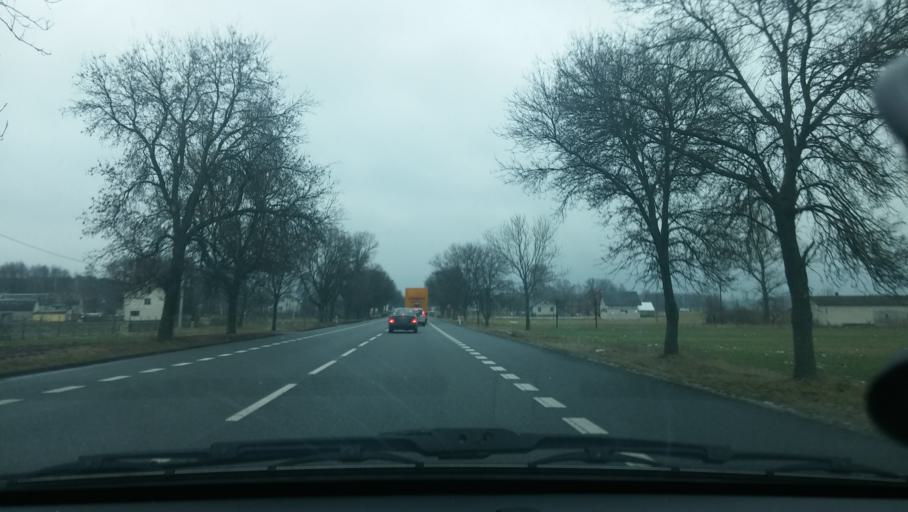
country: PL
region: Masovian Voivodeship
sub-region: Powiat siedlecki
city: Kotun
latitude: 52.1965
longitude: 22.0640
